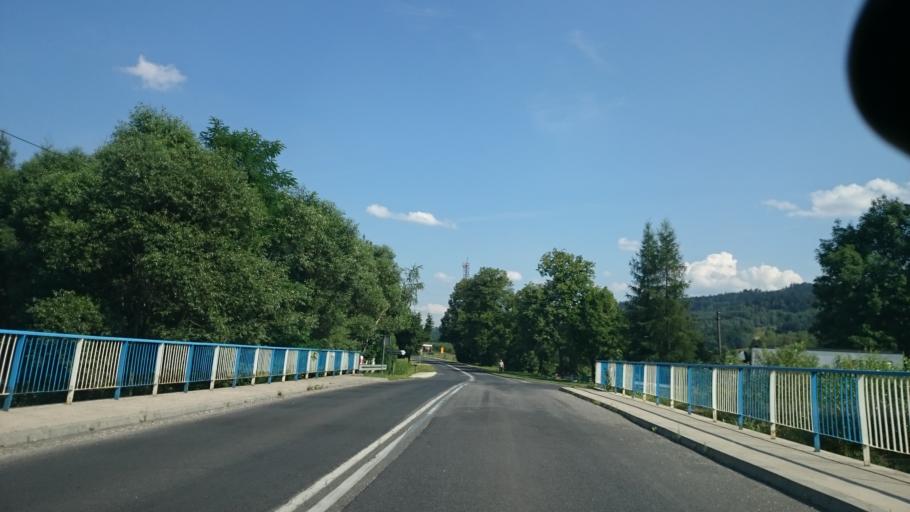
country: PL
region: Lower Silesian Voivodeship
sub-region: Powiat klodzki
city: Ladek-Zdroj
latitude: 50.3482
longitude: 16.7652
